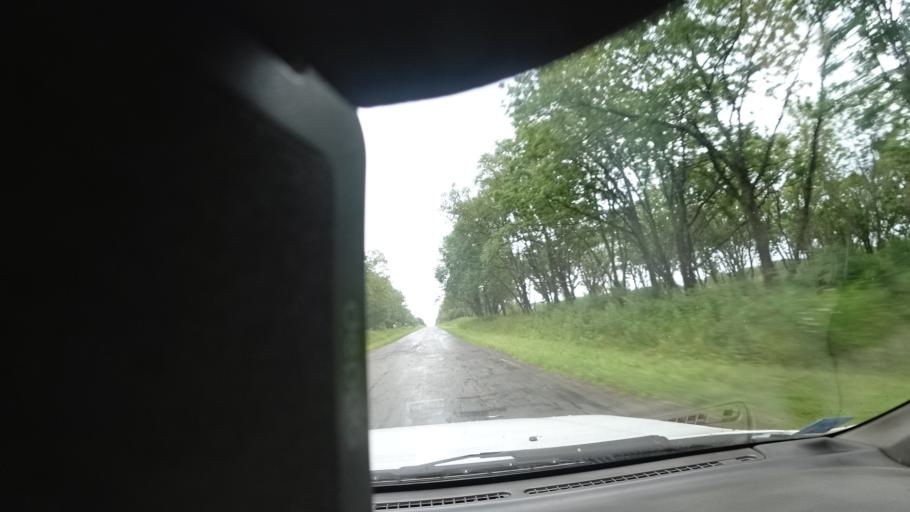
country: RU
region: Primorskiy
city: Lazo
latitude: 45.8701
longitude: 133.7020
